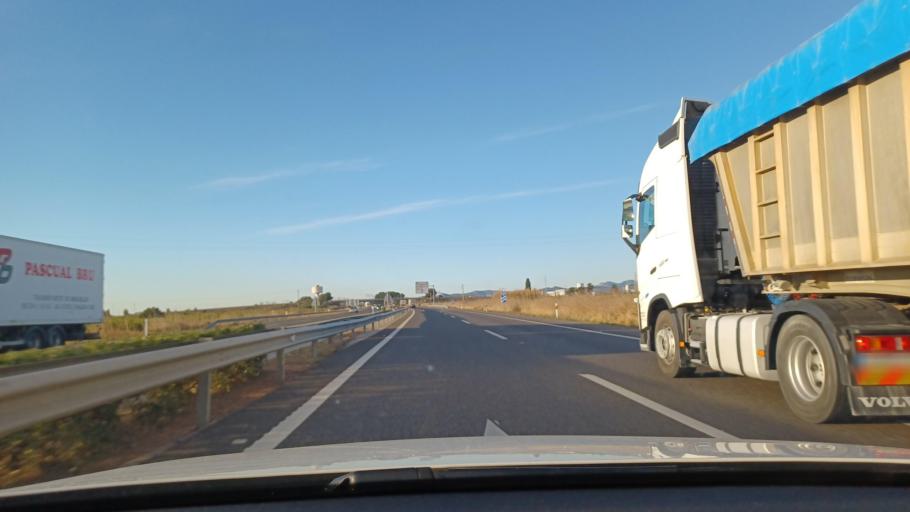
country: ES
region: Valencia
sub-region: Provincia de Castello
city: Moncofar
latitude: 39.8168
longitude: -0.1526
